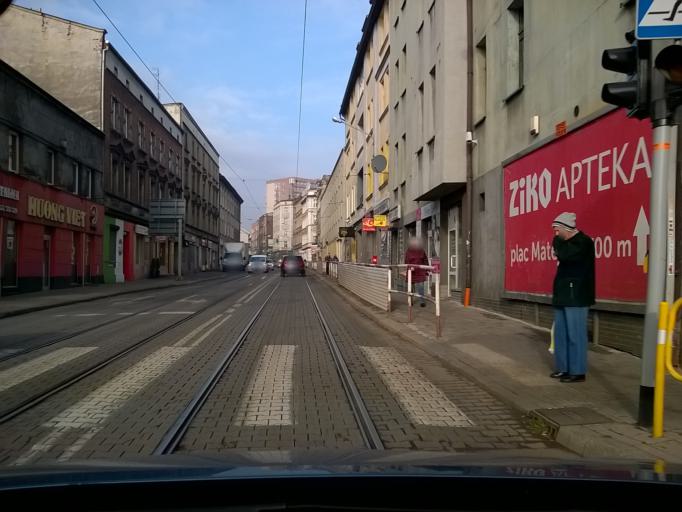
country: PL
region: Silesian Voivodeship
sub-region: Swietochlowice
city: Swietochlowice
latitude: 50.2903
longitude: 18.9465
